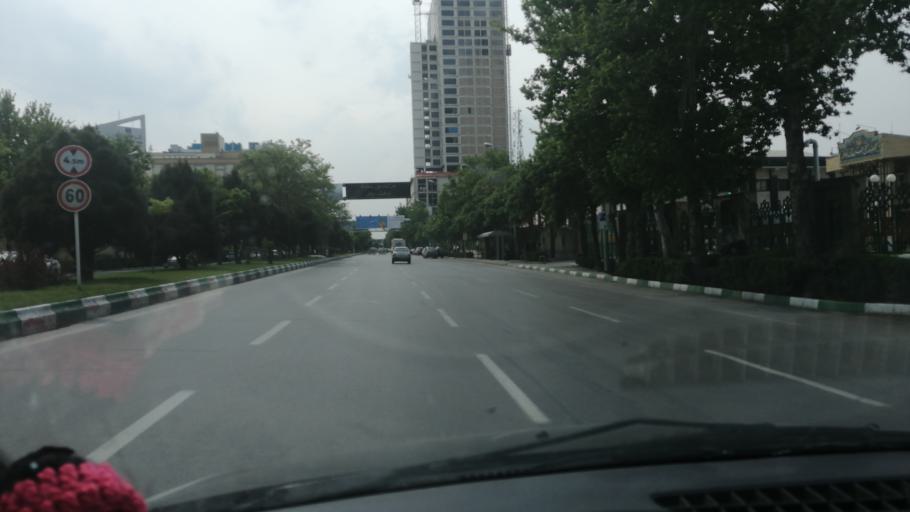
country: IR
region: Razavi Khorasan
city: Mashhad
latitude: 36.3243
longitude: 59.5689
